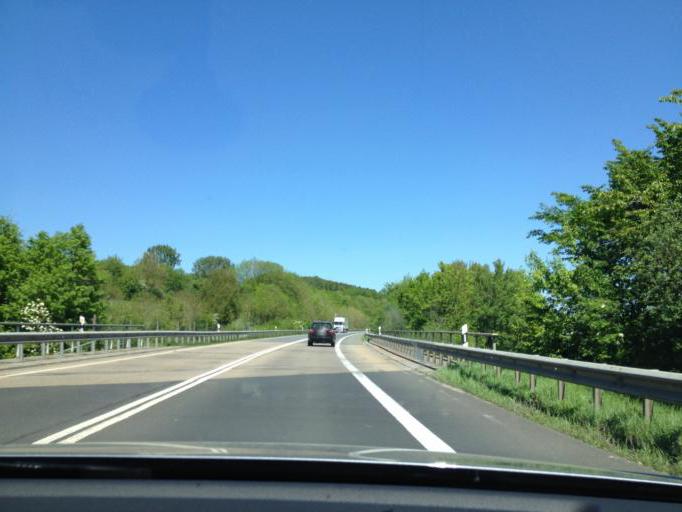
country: DE
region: Rheinland-Pfalz
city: Fliessem
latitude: 50.0282
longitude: 6.5260
